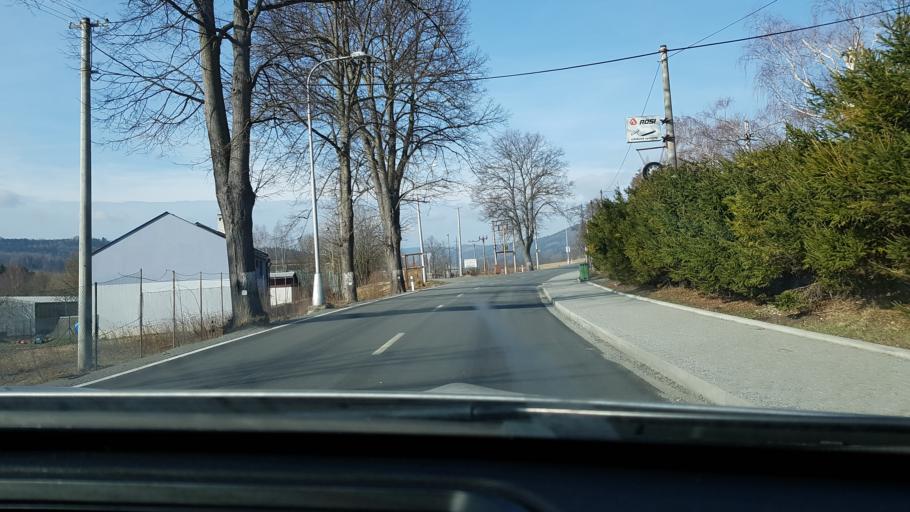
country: CZ
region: Olomoucky
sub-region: Okres Jesenik
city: Jesenik
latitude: 50.2269
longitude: 17.1826
